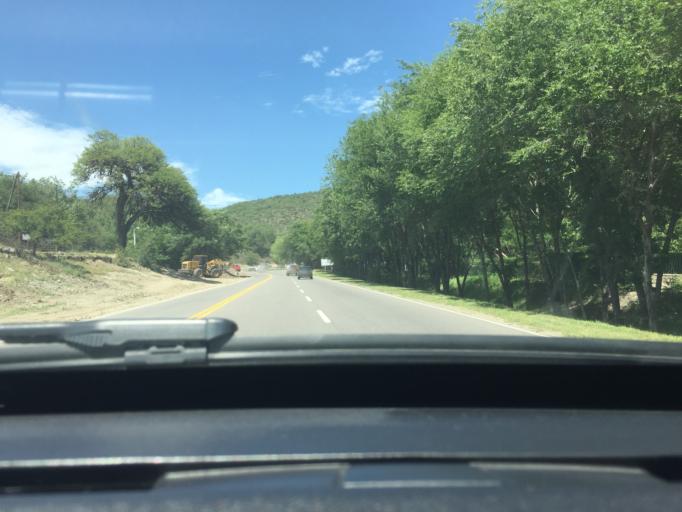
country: AR
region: Cordoba
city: Alta Gracia
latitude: -31.7400
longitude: -64.4537
